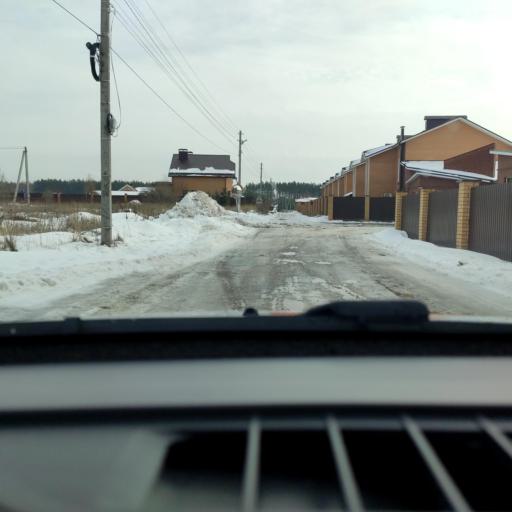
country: RU
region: Voronezj
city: Podgornoye
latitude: 51.7716
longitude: 39.1257
